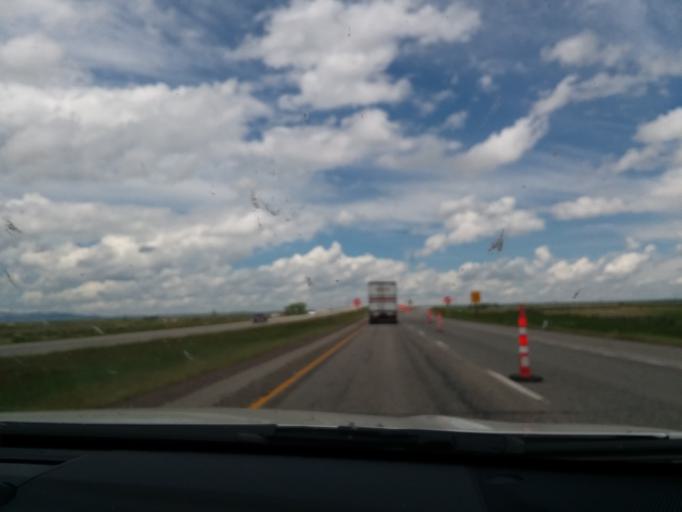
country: US
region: Wyoming
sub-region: Albany County
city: Laramie
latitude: 41.3902
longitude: -105.8201
